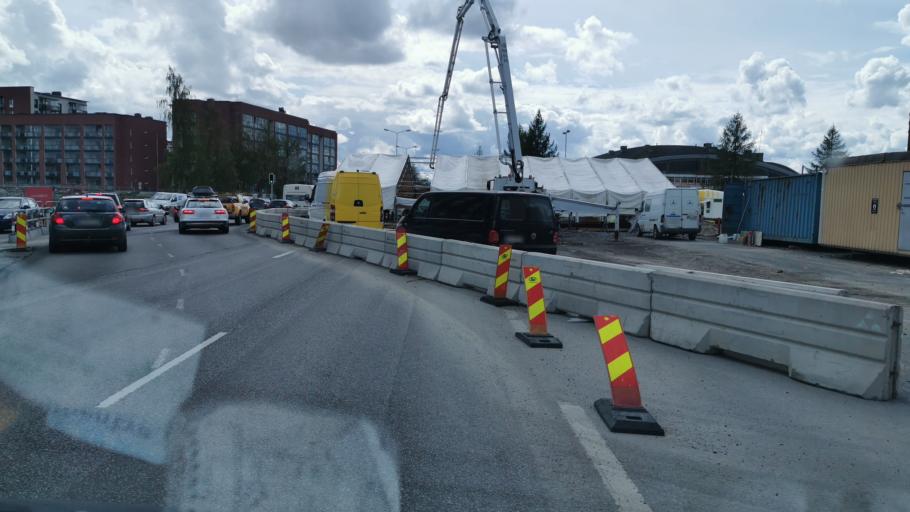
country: FI
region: Northern Ostrobothnia
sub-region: Oulu
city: Oulu
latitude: 65.0014
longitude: 25.4635
